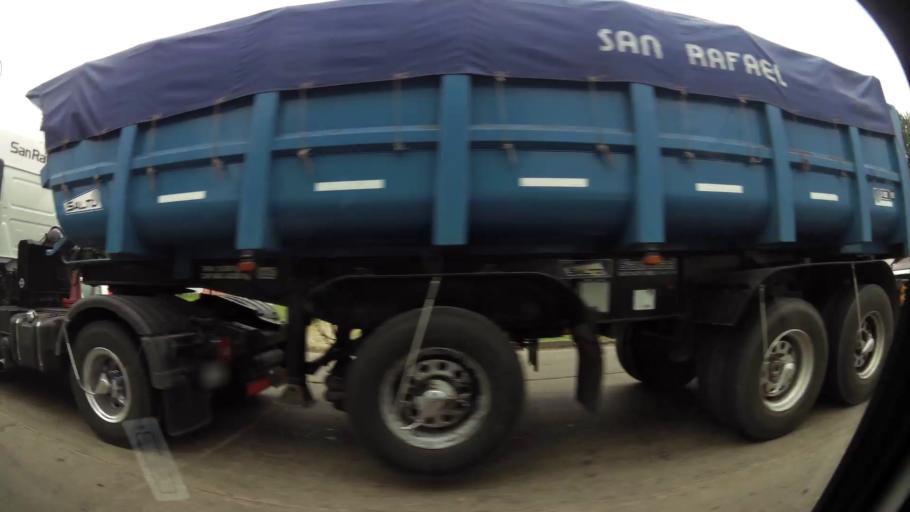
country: AR
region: Buenos Aires
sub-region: Partido de La Plata
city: La Plata
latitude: -34.8832
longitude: -57.9747
